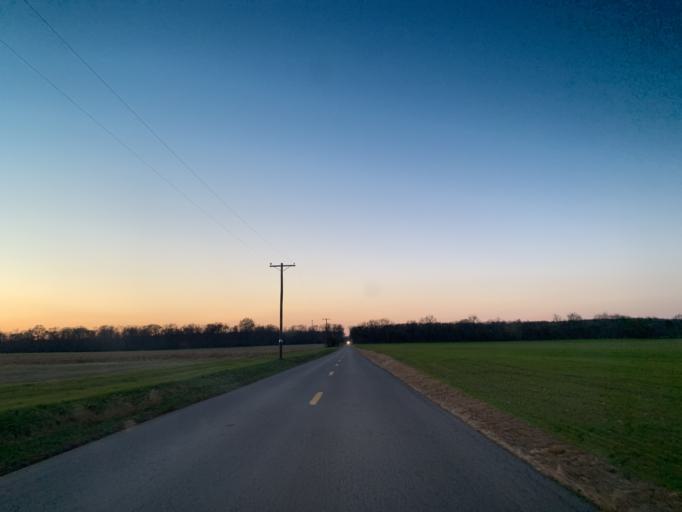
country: US
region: Delaware
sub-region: New Castle County
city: Middletown
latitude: 39.4112
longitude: -75.7524
